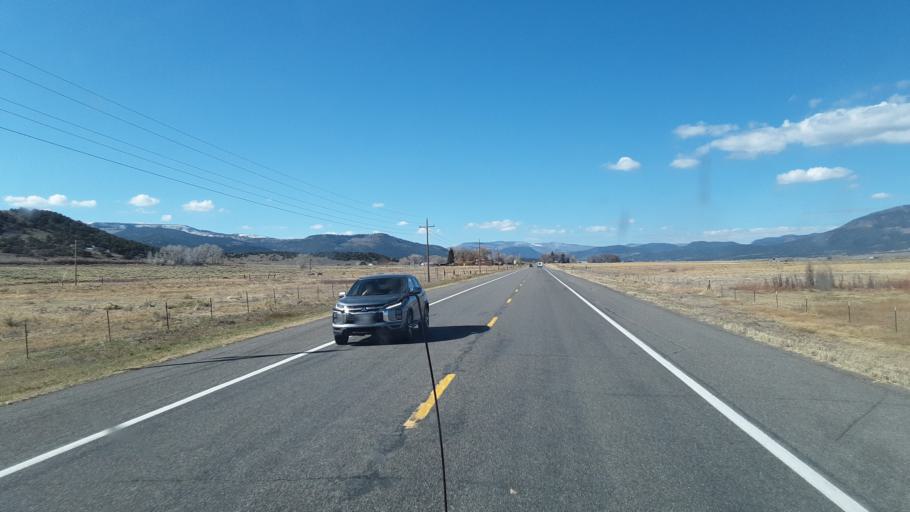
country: US
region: Colorado
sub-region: Rio Grande County
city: Del Norte
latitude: 37.6769
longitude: -106.4626
